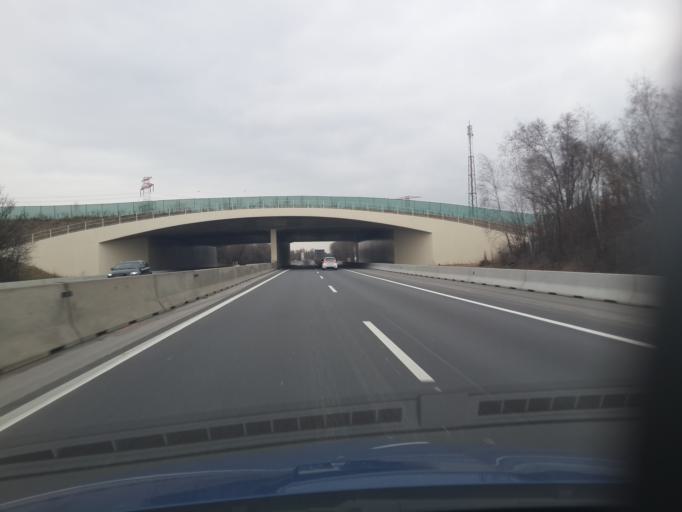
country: AT
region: Lower Austria
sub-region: Politischer Bezirk Ganserndorf
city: Orth an der Donau
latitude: 48.0716
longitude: 16.6859
